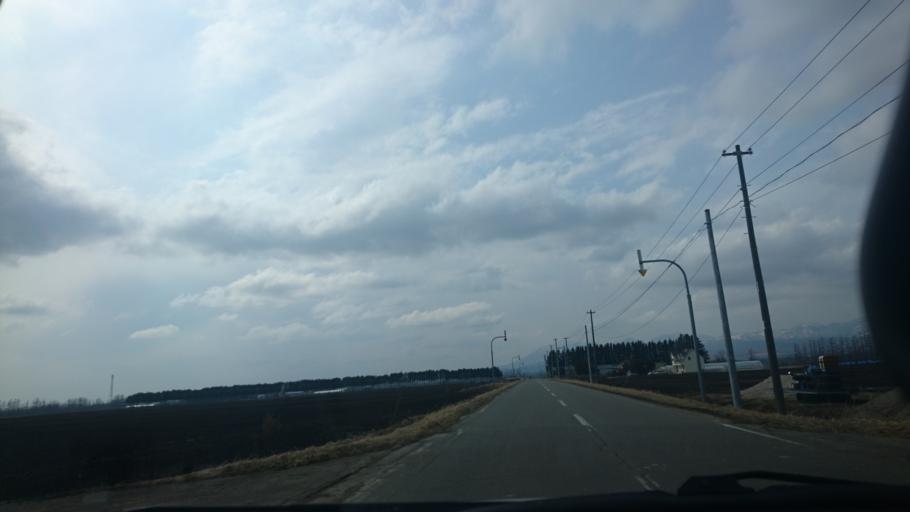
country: JP
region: Hokkaido
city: Otofuke
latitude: 43.2152
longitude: 143.2902
